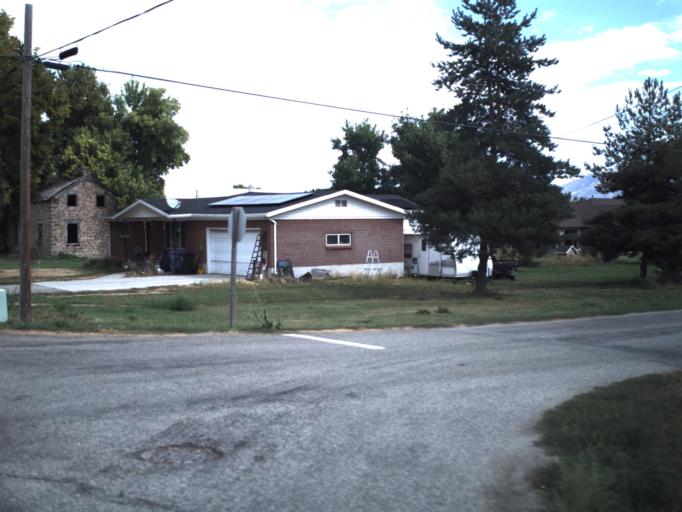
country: US
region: Utah
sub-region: Cache County
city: Wellsville
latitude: 41.6324
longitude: -111.9346
